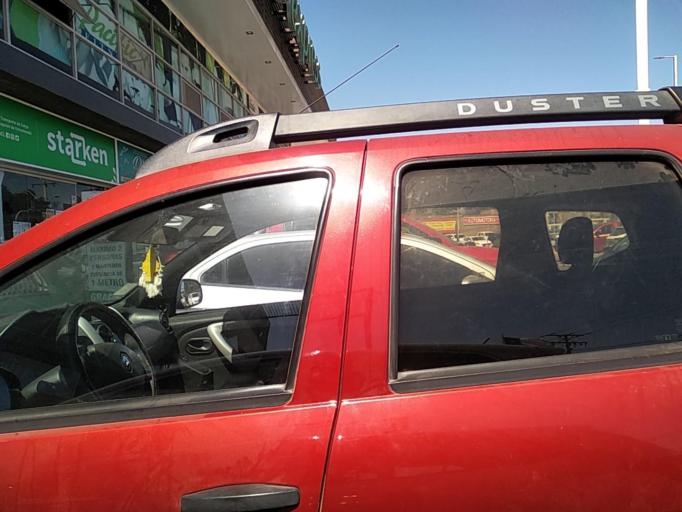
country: CL
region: Atacama
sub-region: Provincia de Copiapo
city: Copiapo
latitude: -27.3980
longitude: -70.2944
